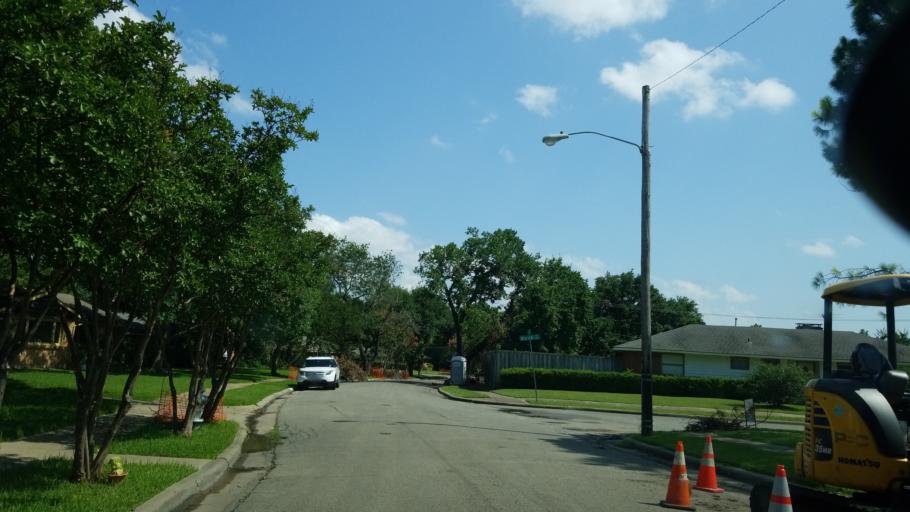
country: US
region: Texas
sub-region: Dallas County
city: Farmers Branch
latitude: 32.8889
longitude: -96.8574
